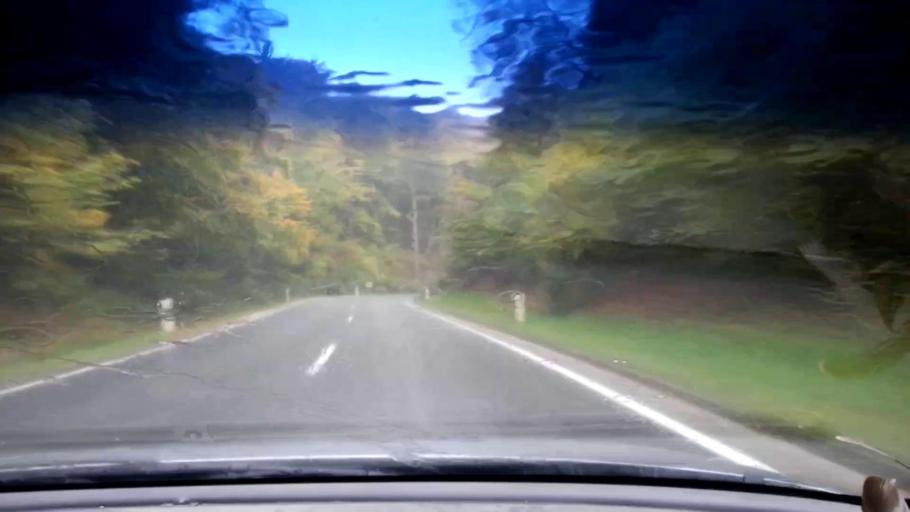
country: DE
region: Bavaria
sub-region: Upper Franconia
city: Wattendorf
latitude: 50.0266
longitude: 11.1063
